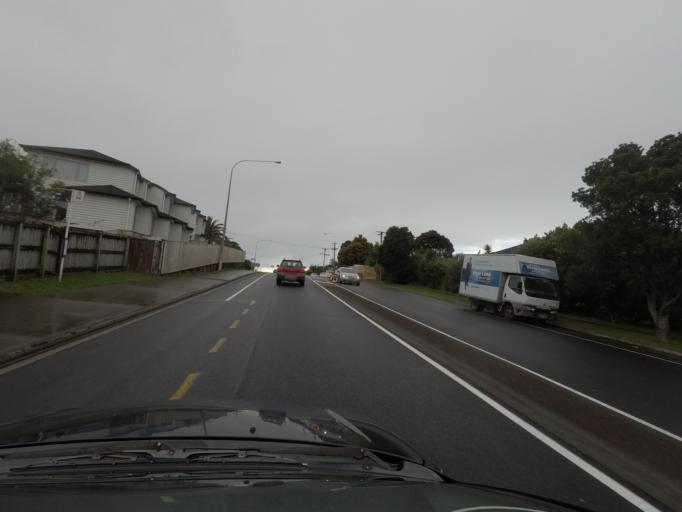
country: NZ
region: Auckland
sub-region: Auckland
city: Rothesay Bay
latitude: -36.7289
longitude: 174.7263
